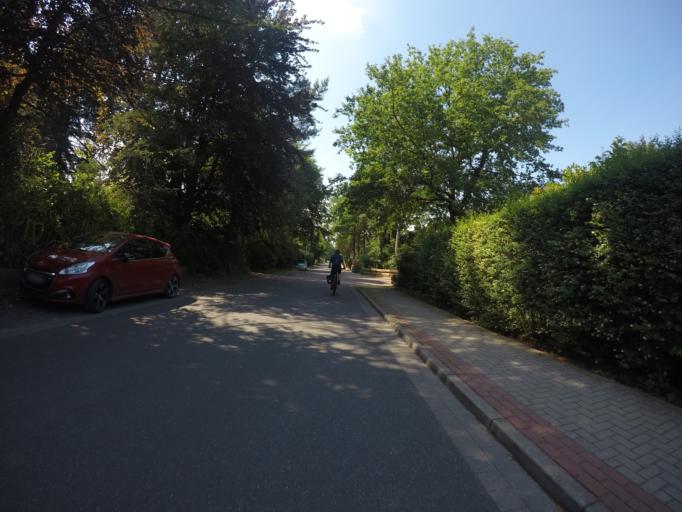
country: DE
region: Lower Saxony
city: Buchholz in der Nordheide
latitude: 53.3270
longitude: 9.8443
